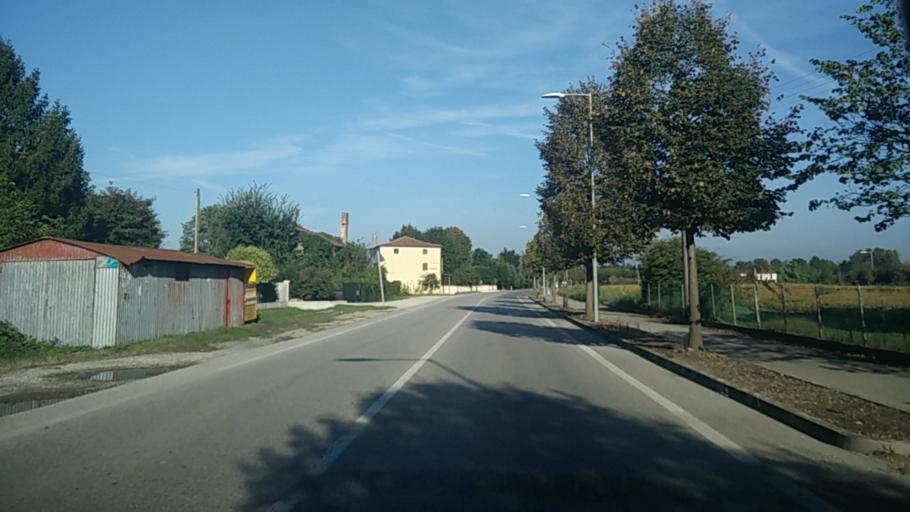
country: IT
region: Veneto
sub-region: Provincia di Padova
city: Trebaseleghe
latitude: 45.6032
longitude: 12.0301
